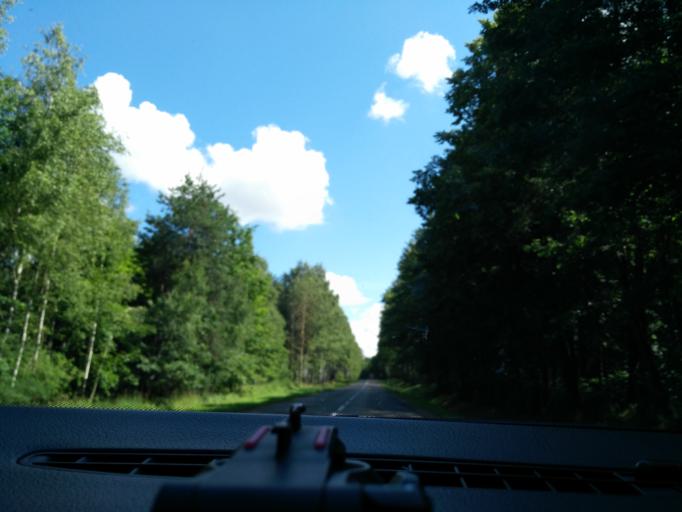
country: PL
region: Masovian Voivodeship
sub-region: Powiat losicki
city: Losice
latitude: 52.2462
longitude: 22.7837
